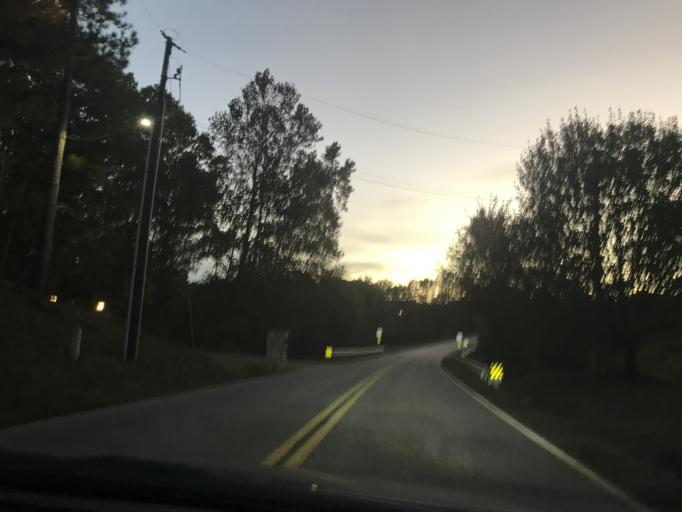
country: US
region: South Carolina
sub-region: Spartanburg County
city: Mayo
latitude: 35.0899
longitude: -81.8871
